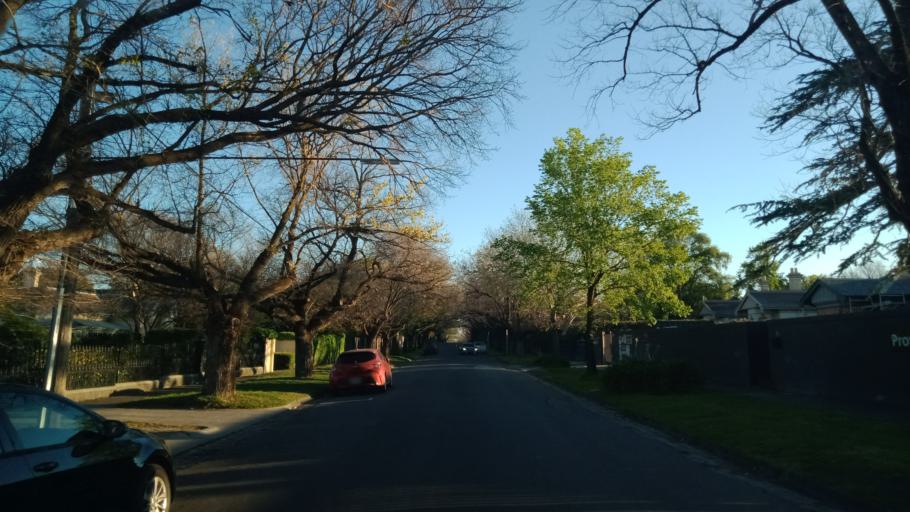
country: AU
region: Victoria
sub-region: Boroondara
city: Hawthorn East
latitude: -37.8305
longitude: 145.0388
